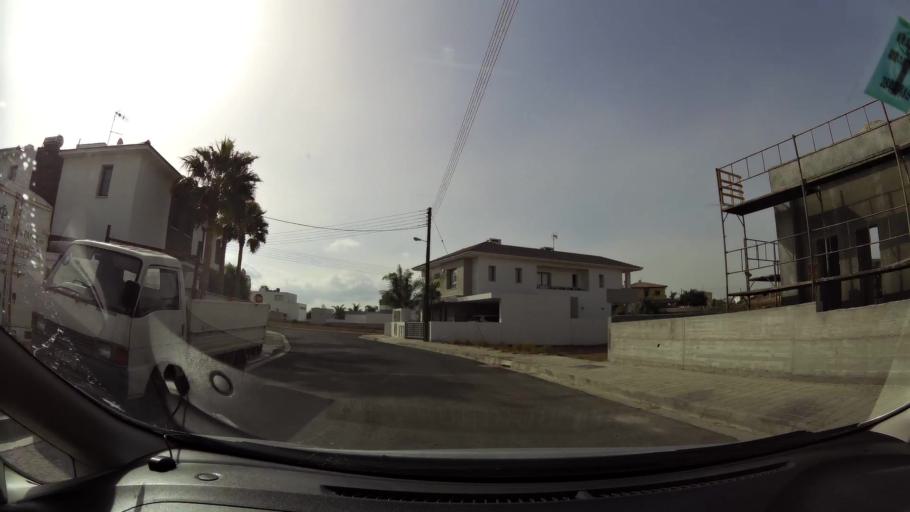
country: CY
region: Lefkosia
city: Geri
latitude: 35.0720
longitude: 33.3945
